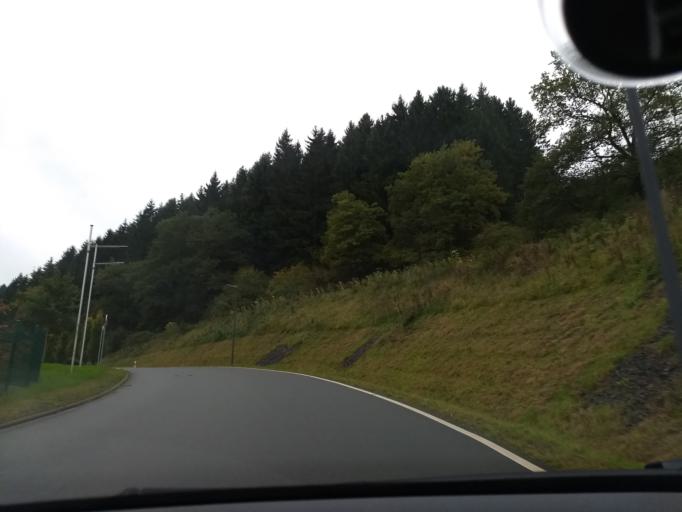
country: DE
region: North Rhine-Westphalia
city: Eslohe
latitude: 51.2286
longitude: 8.1295
